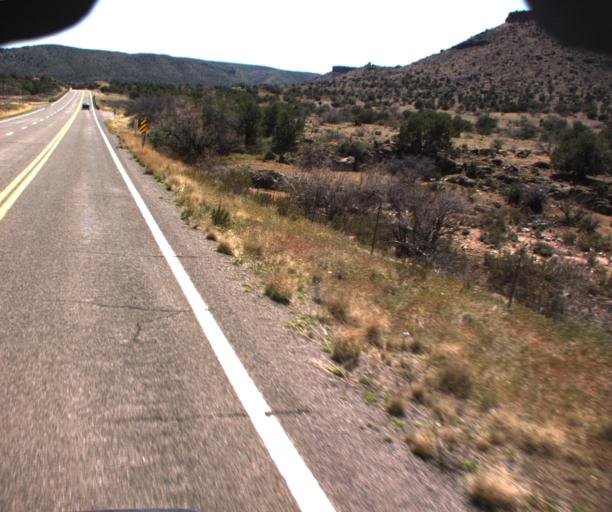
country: US
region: Arizona
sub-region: Mohave County
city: Peach Springs
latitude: 35.4382
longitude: -113.6462
